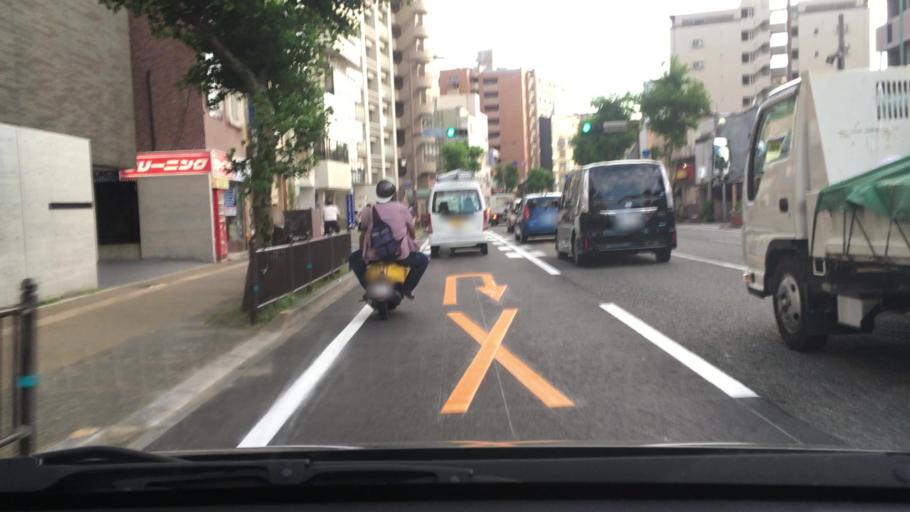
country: JP
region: Fukuoka
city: Fukuoka-shi
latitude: 33.5798
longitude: 130.3812
